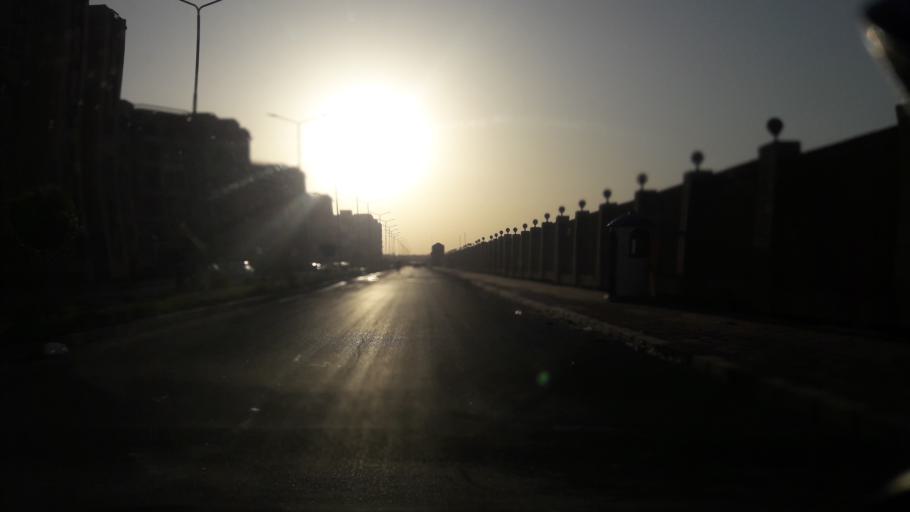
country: EG
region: Al Jizah
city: Madinat Sittah Uktubar
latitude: 29.9582
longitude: 31.0437
